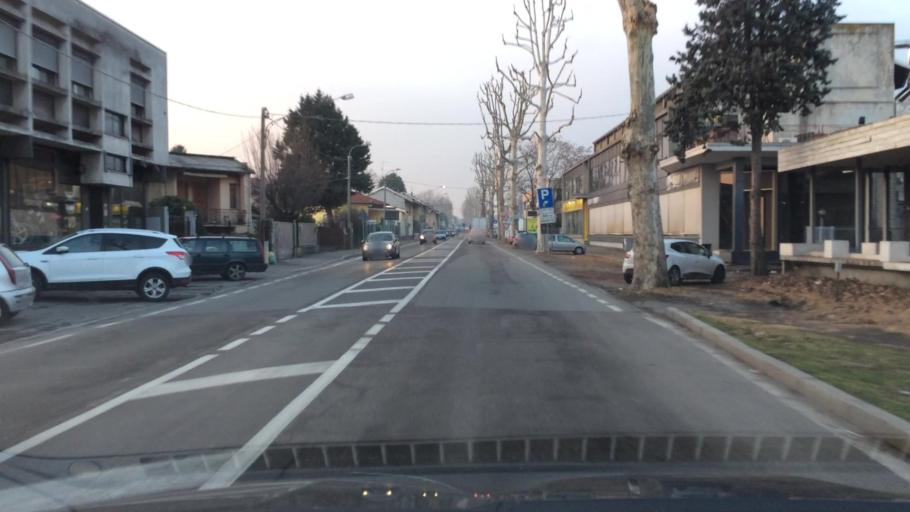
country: IT
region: Lombardy
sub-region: Provincia di Varese
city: Saronno
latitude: 45.6136
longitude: 9.0343
